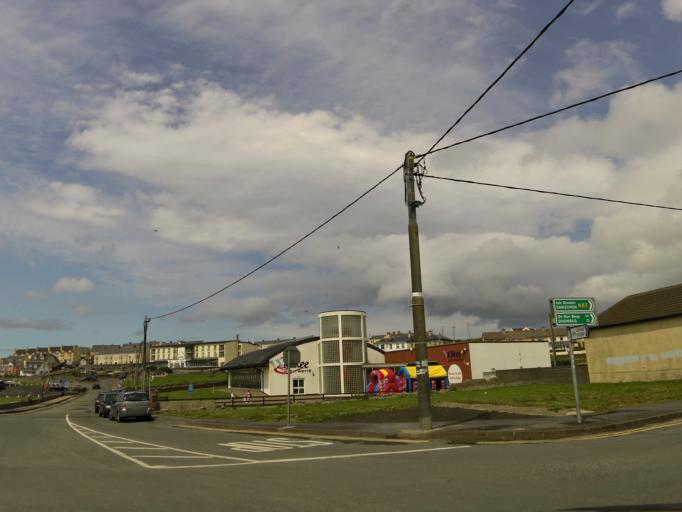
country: IE
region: Munster
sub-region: An Clar
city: Kilrush
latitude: 52.6824
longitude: -9.6459
